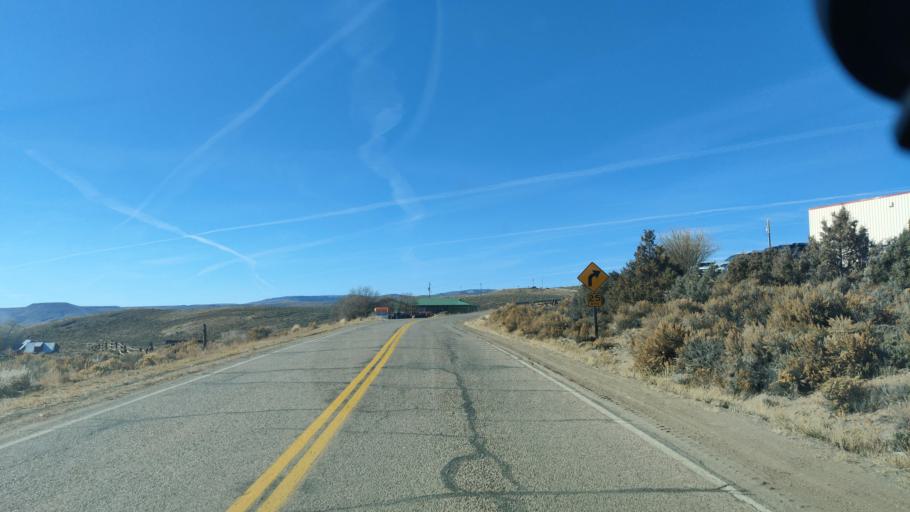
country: US
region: Colorado
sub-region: Gunnison County
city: Gunnison
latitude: 38.5317
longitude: -106.9560
